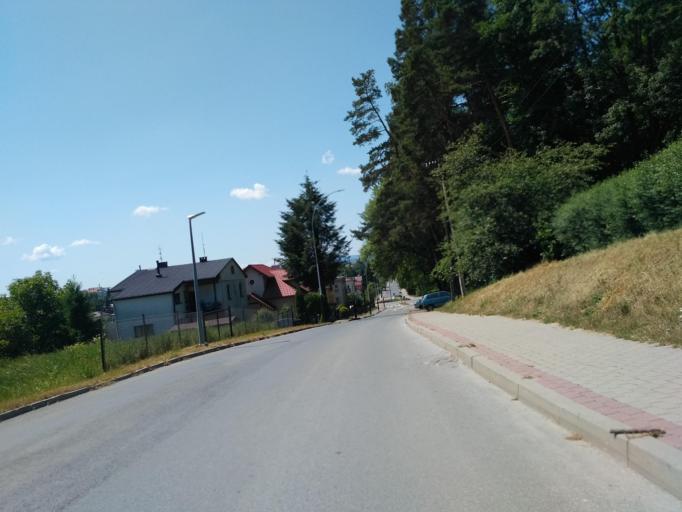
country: PL
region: Subcarpathian Voivodeship
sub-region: Krosno
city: Krosno
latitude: 49.7017
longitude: 21.7660
